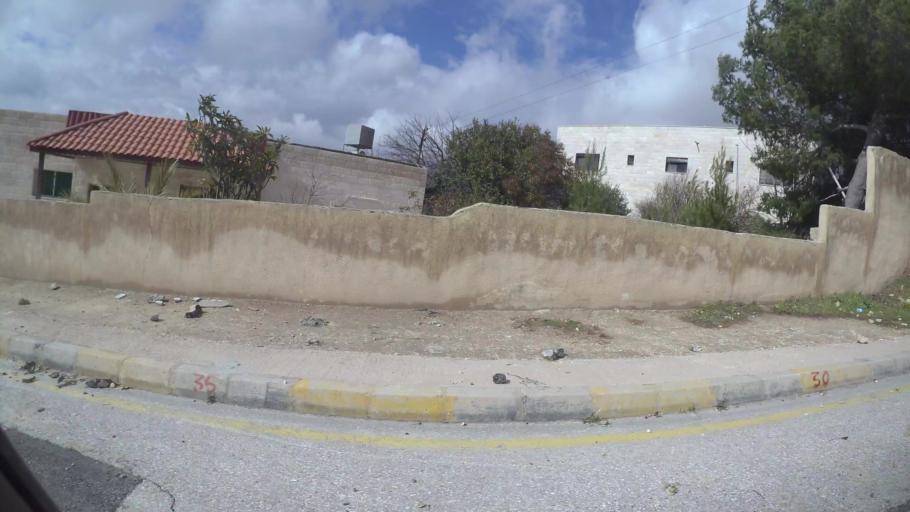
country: JO
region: Amman
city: Al Jubayhah
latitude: 32.0726
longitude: 35.8786
